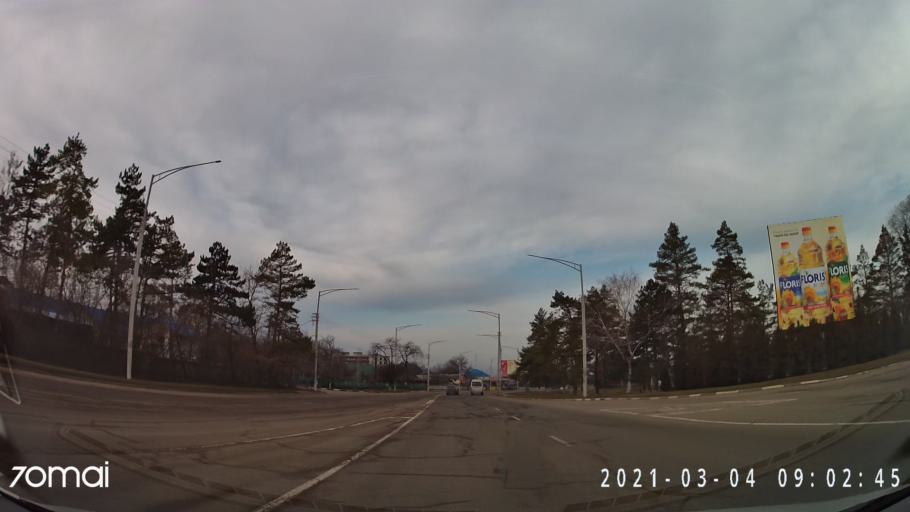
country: MD
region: Balti
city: Balti
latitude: 47.7453
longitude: 27.9519
